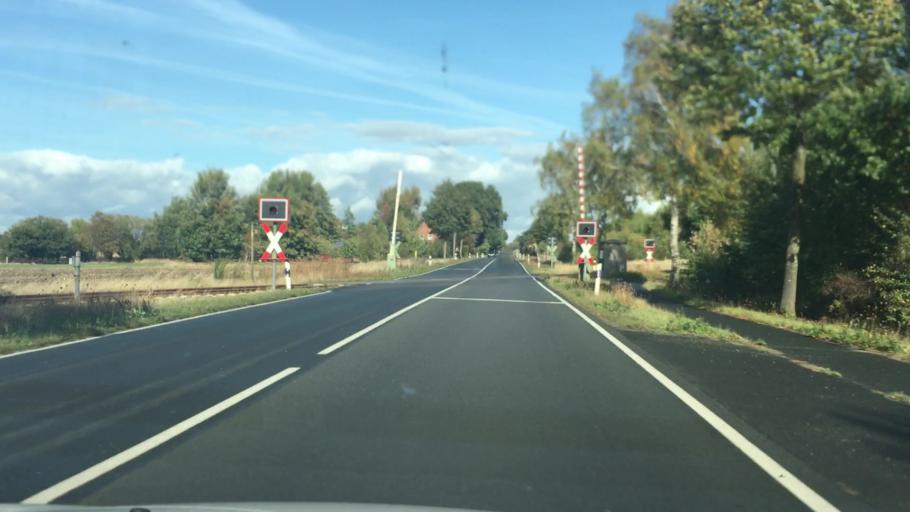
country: DE
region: Lower Saxony
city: Sulingen
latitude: 52.6626
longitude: 8.7724
